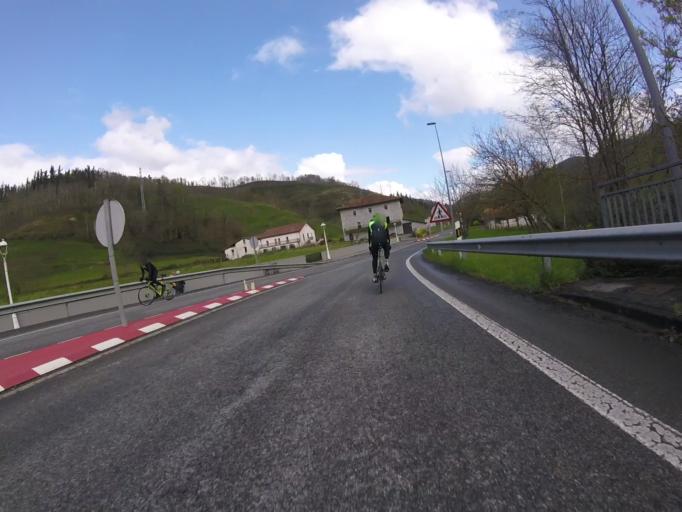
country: ES
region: Basque Country
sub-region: Provincia de Guipuzcoa
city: Amezqueta
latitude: 43.0536
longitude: -2.0887
